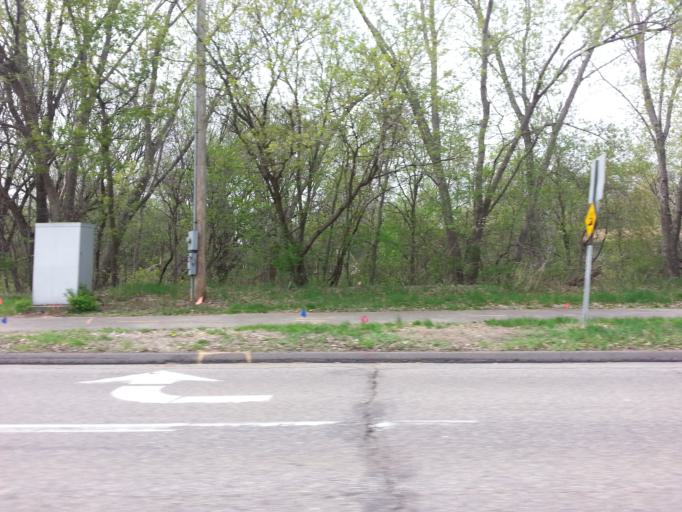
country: US
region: Minnesota
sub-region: Hennepin County
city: Edina
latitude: 44.8502
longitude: -93.3709
